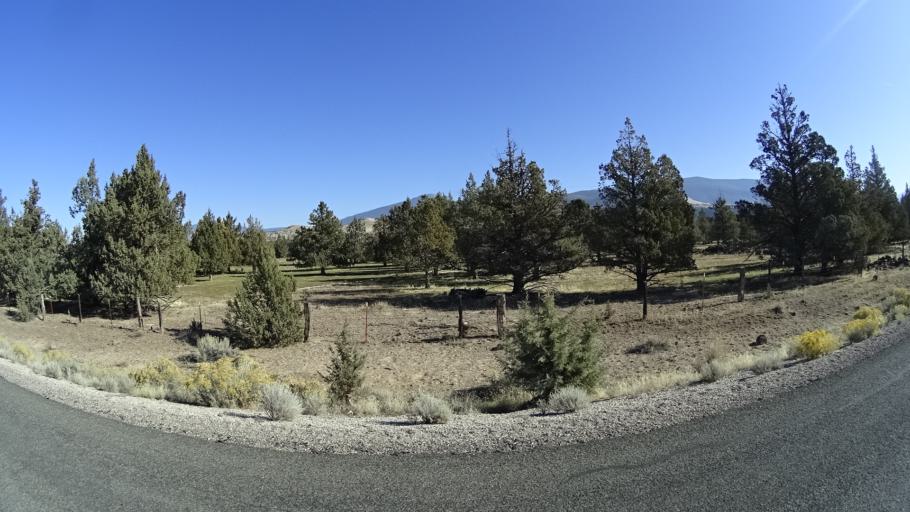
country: US
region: California
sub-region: Siskiyou County
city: Montague
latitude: 41.6570
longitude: -122.3647
